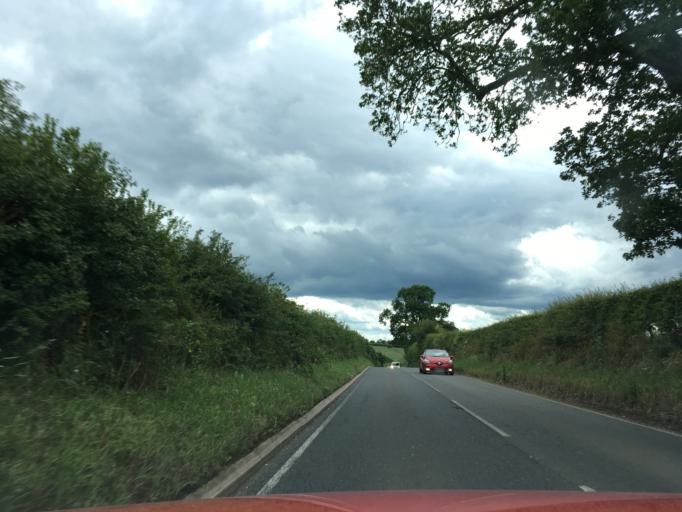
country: GB
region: England
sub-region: Central Bedfordshire
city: Woburn
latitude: 51.9788
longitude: -0.6383
